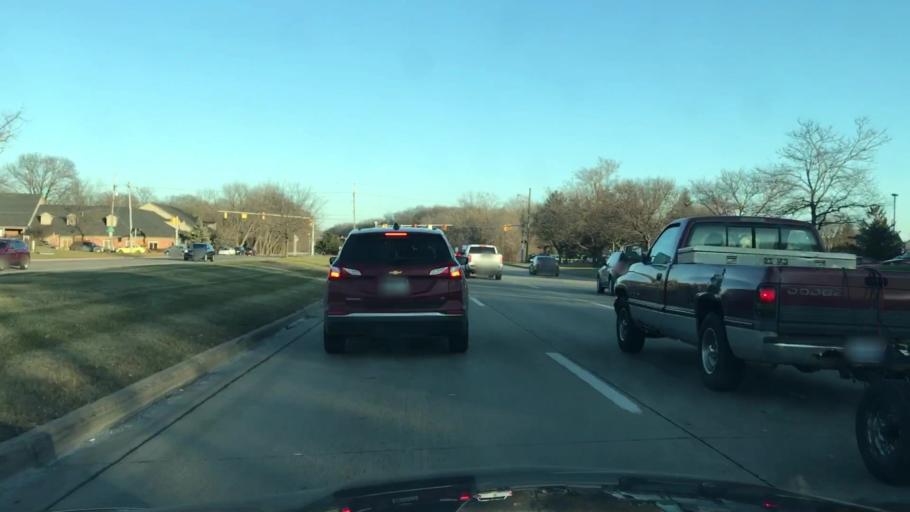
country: US
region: Michigan
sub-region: Macomb County
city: Fraser
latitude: 42.5664
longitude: -82.9696
